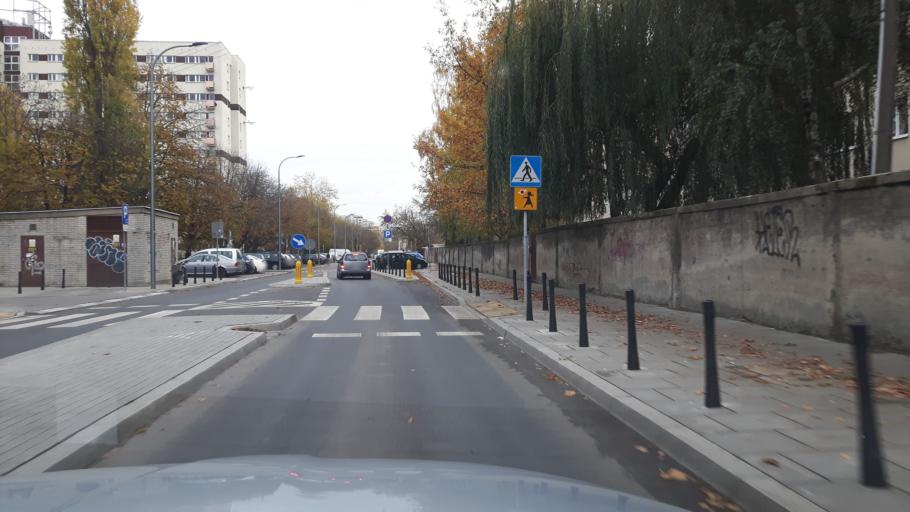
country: PL
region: Masovian Voivodeship
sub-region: Warszawa
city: Mokotow
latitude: 52.1688
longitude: 21.0009
